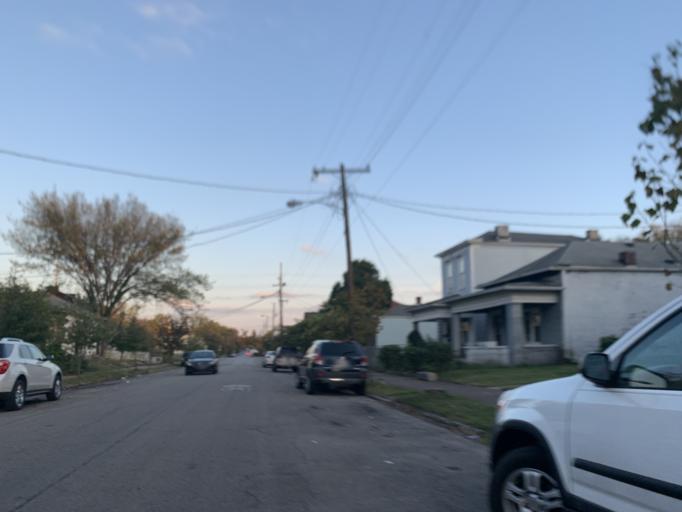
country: US
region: Kentucky
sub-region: Jefferson County
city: Louisville
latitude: 38.2535
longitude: -85.7892
